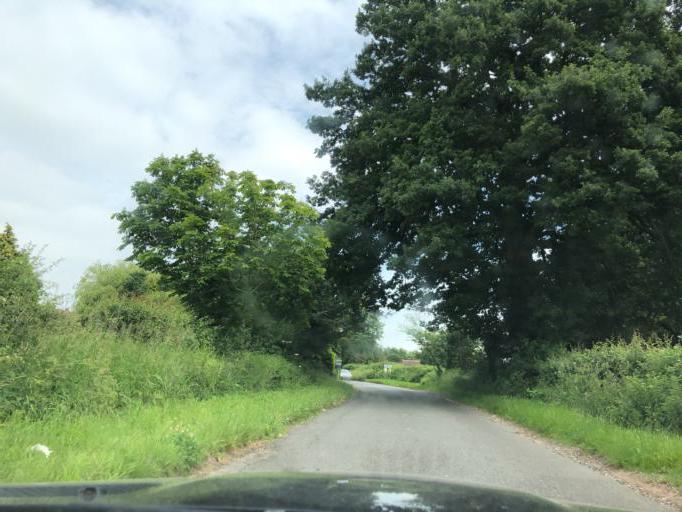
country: GB
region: England
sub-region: Warwickshire
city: Royal Leamington Spa
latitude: 52.3162
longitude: -1.5602
